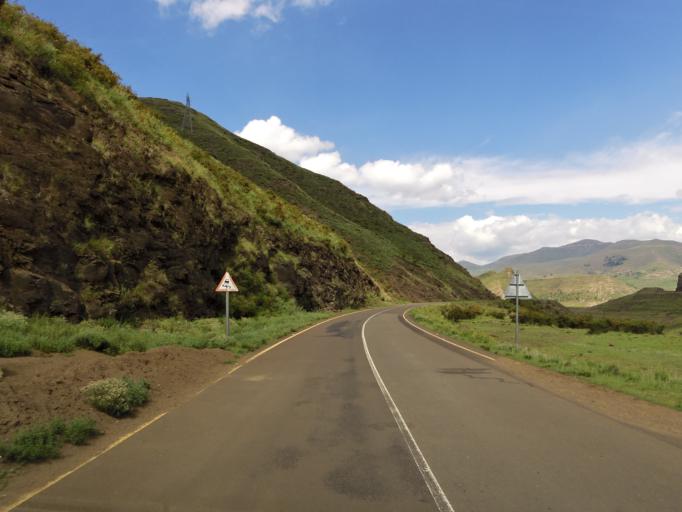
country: LS
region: Thaba-Tseka
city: Thaba-Tseka
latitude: -29.1582
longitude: 28.4748
